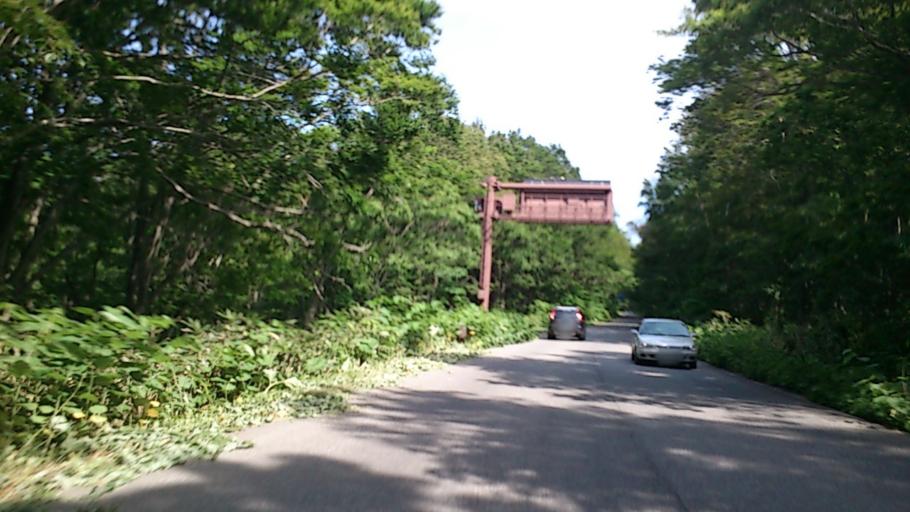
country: JP
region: Aomori
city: Aomori Shi
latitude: 40.6996
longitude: 140.8334
